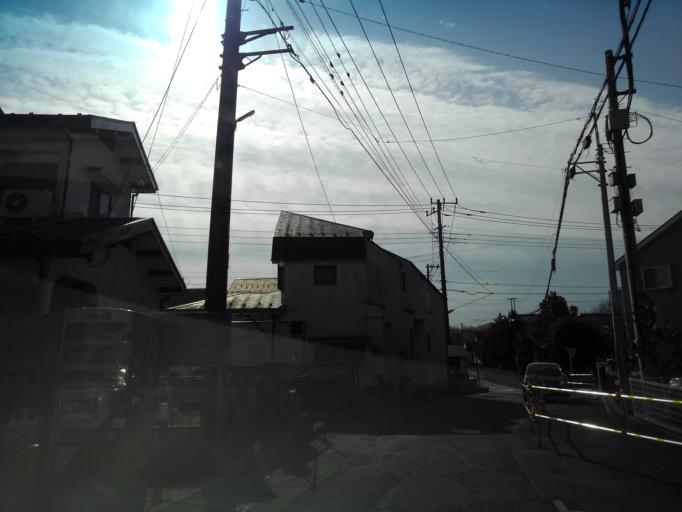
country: JP
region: Saitama
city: Tokorozawa
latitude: 35.7893
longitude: 139.5125
